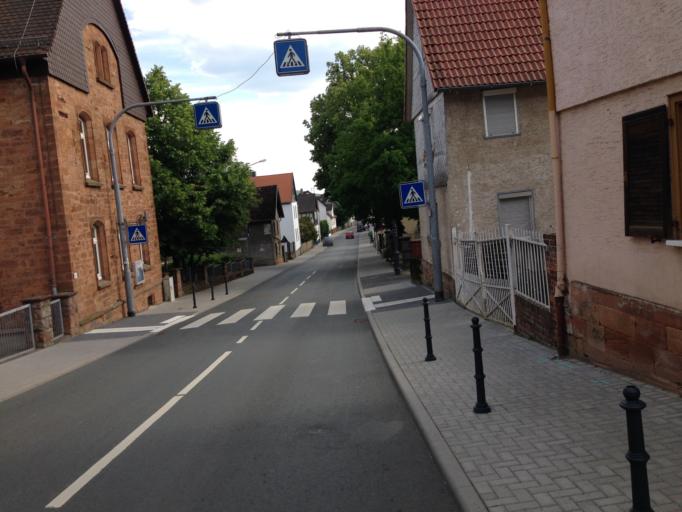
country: DE
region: Hesse
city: Staufenberg
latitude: 50.6628
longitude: 8.7278
